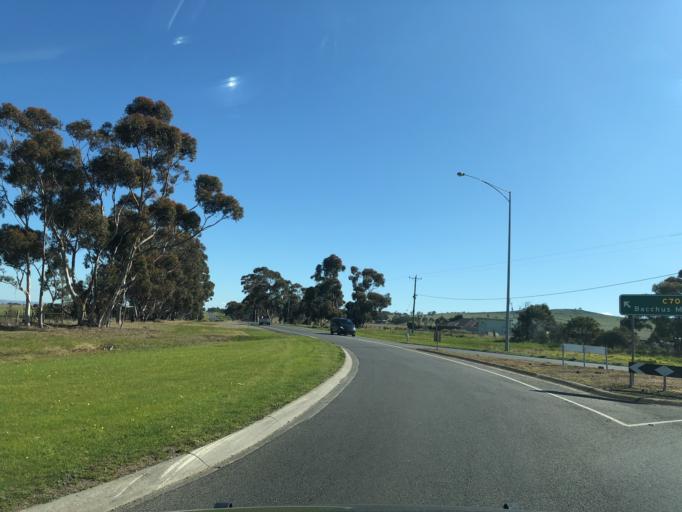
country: AU
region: Victoria
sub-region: Melton
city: Kurunjang
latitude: -37.6089
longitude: 144.5908
